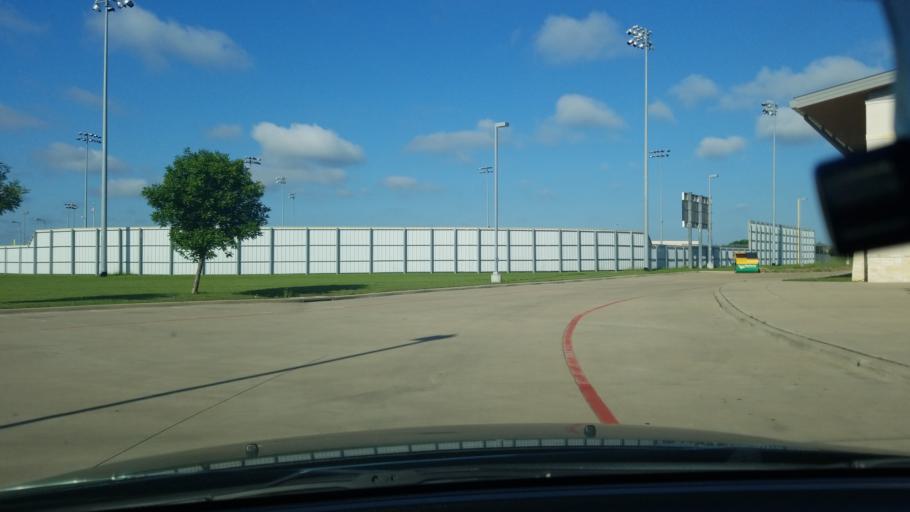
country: US
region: Texas
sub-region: Dallas County
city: Sunnyvale
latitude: 32.8013
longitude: -96.5563
